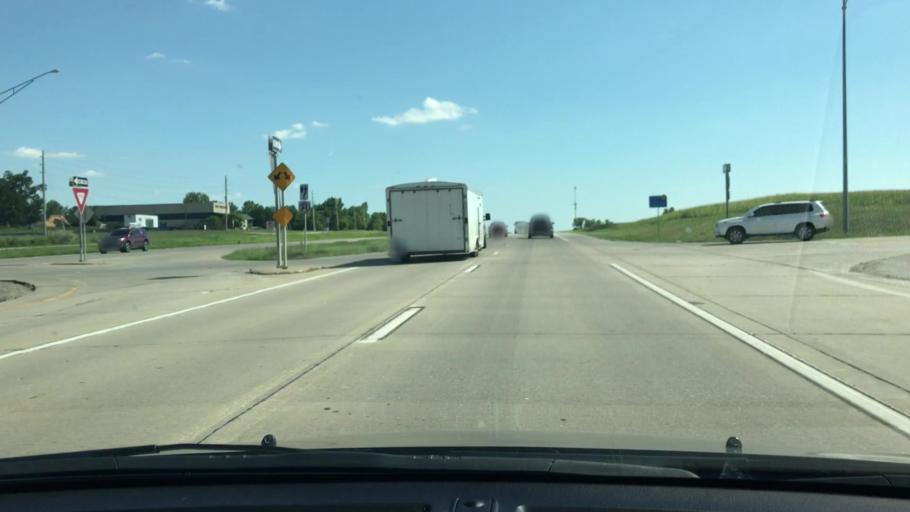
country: US
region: Missouri
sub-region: Jackson County
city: Lees Summit
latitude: 38.8782
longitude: -94.3743
